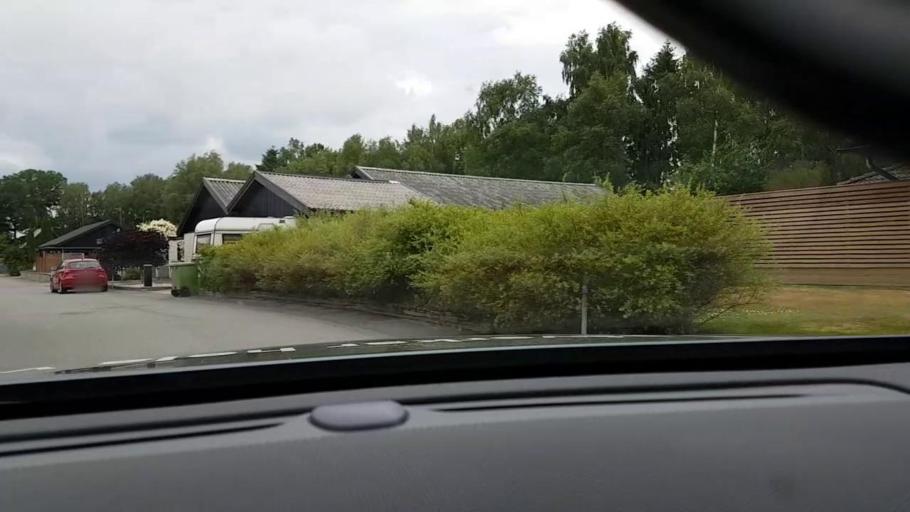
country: SE
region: Skane
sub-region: Hassleholms Kommun
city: Hassleholm
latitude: 56.1725
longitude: 13.8015
